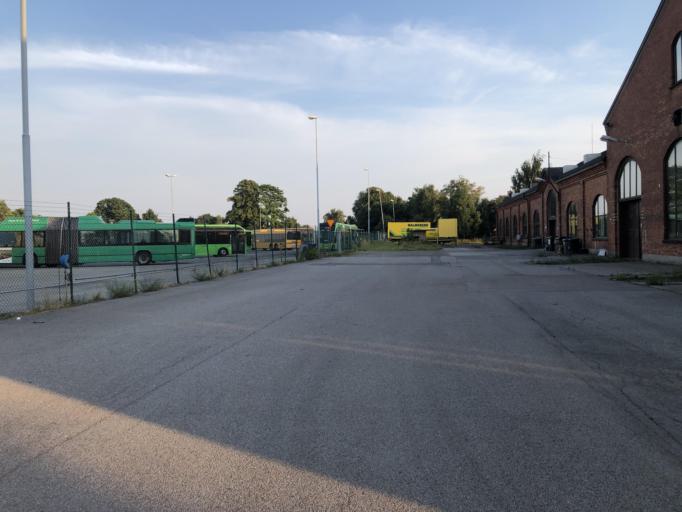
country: SE
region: Skane
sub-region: Burlovs Kommun
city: Arloev
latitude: 55.6064
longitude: 13.0442
